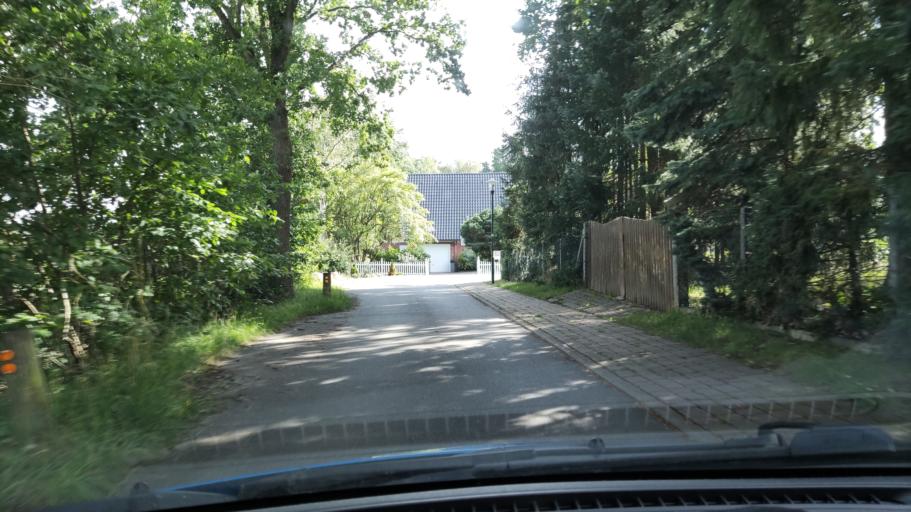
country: DE
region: Lower Saxony
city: Salzhausen
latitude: 53.2252
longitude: 10.1532
